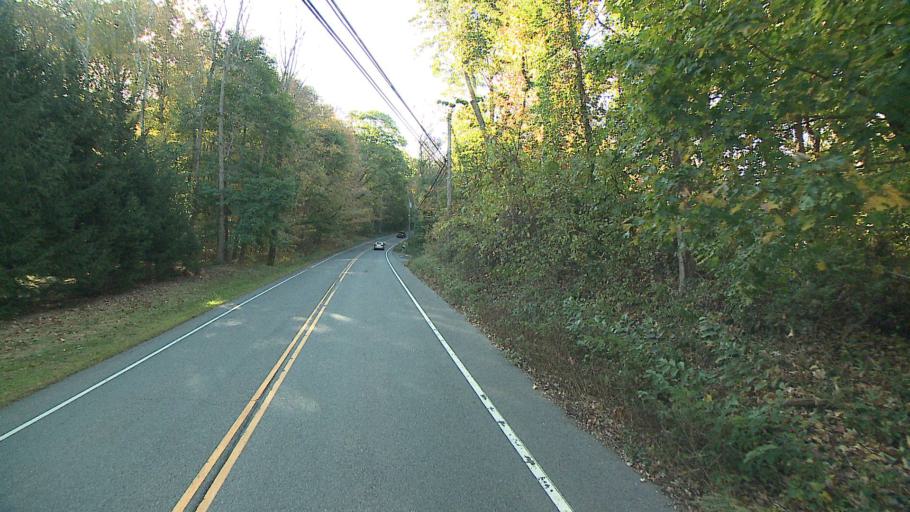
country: US
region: Connecticut
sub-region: Fairfield County
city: Bethel
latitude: 41.3538
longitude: -73.4148
